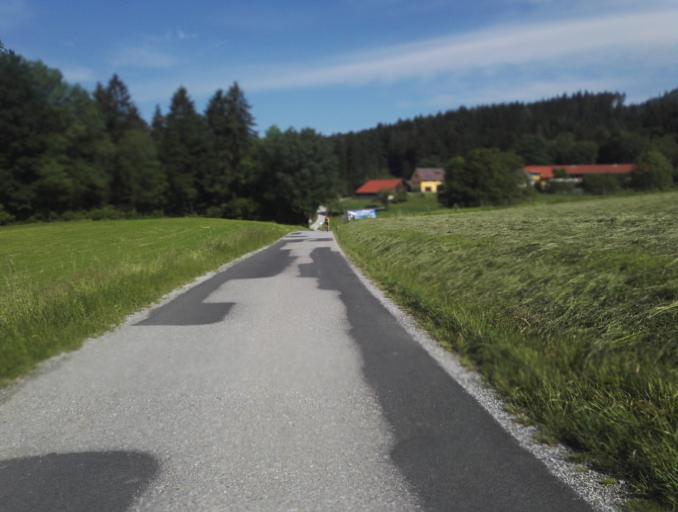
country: AT
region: Styria
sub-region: Politischer Bezirk Graz-Umgebung
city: Stattegg
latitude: 47.1615
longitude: 15.4294
